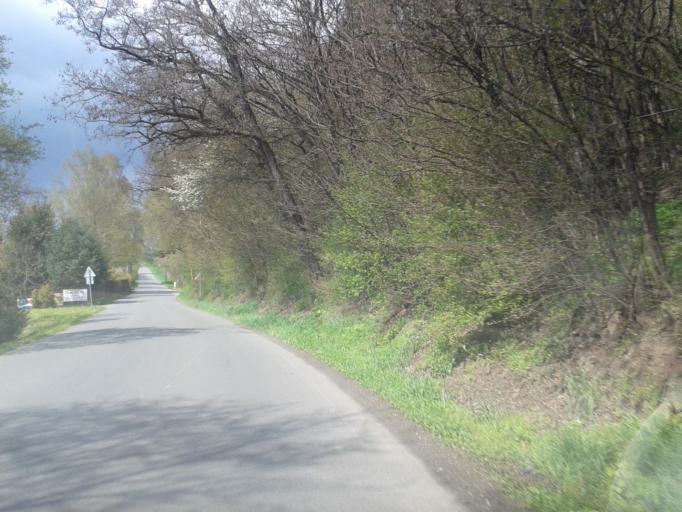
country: CZ
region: Central Bohemia
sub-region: Okres Beroun
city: Kraluv Dvur
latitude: 49.9588
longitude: 14.0085
